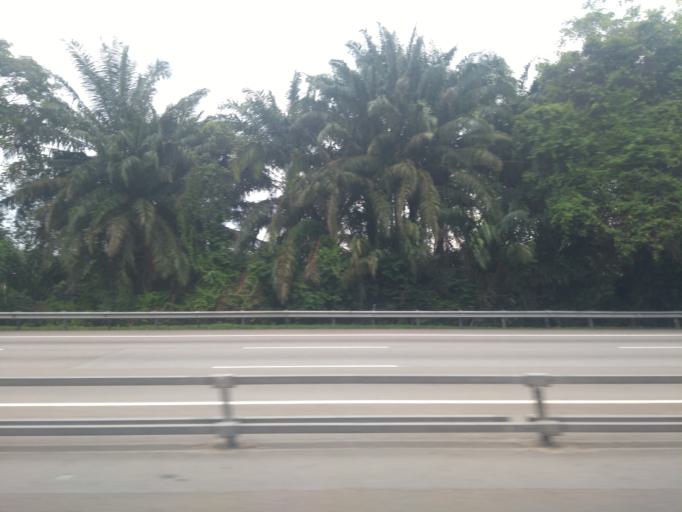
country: MY
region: Melaka
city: Alor Gajah
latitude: 2.3840
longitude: 102.2301
